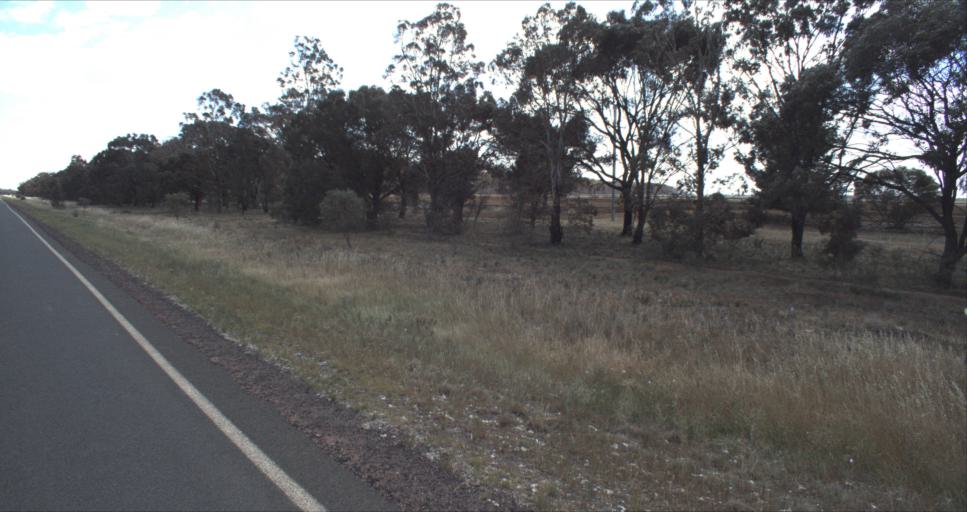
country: AU
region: New South Wales
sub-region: Murrumbidgee Shire
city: Darlington Point
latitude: -34.5892
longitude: 146.1638
